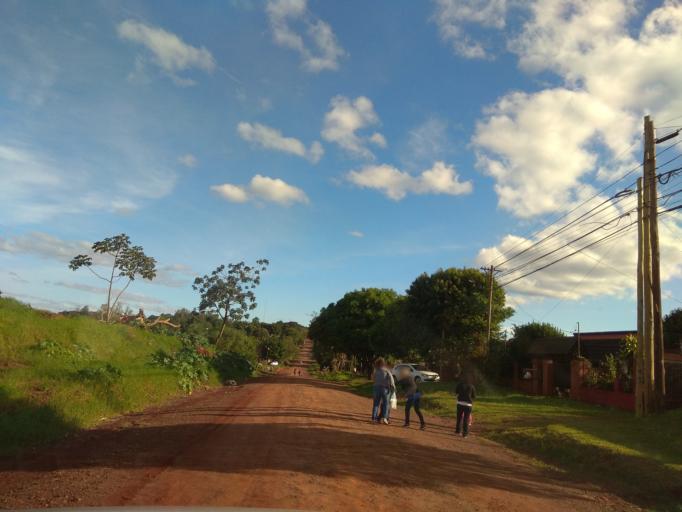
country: AR
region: Misiones
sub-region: Departamento de Capital
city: Posadas
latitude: -27.3932
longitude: -55.9277
